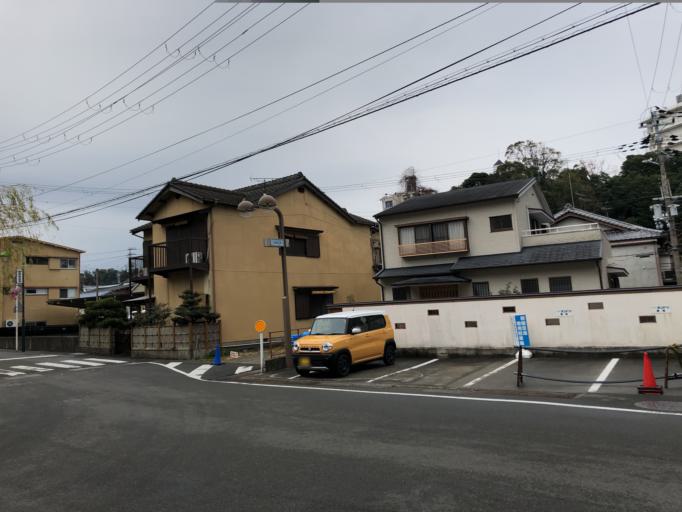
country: JP
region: Wakayama
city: Tanabe
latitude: 33.6832
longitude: 135.3477
